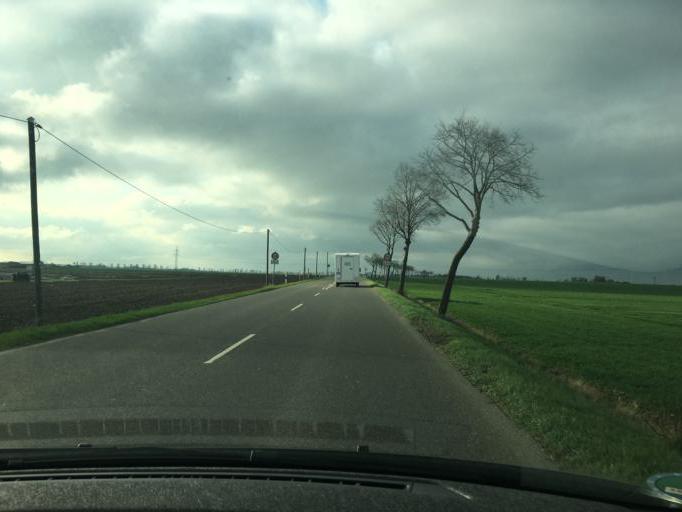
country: DE
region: North Rhine-Westphalia
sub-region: Regierungsbezirk Koln
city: Vettweiss
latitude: 50.7750
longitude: 6.5909
